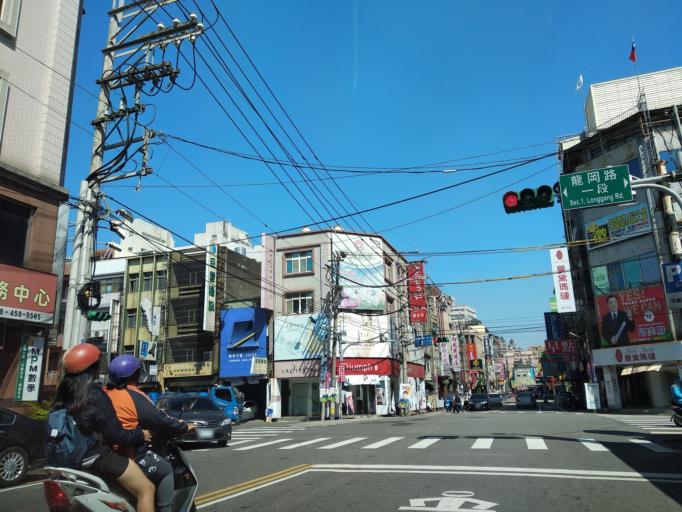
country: TW
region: Taiwan
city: Taoyuan City
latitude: 24.9498
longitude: 121.2234
